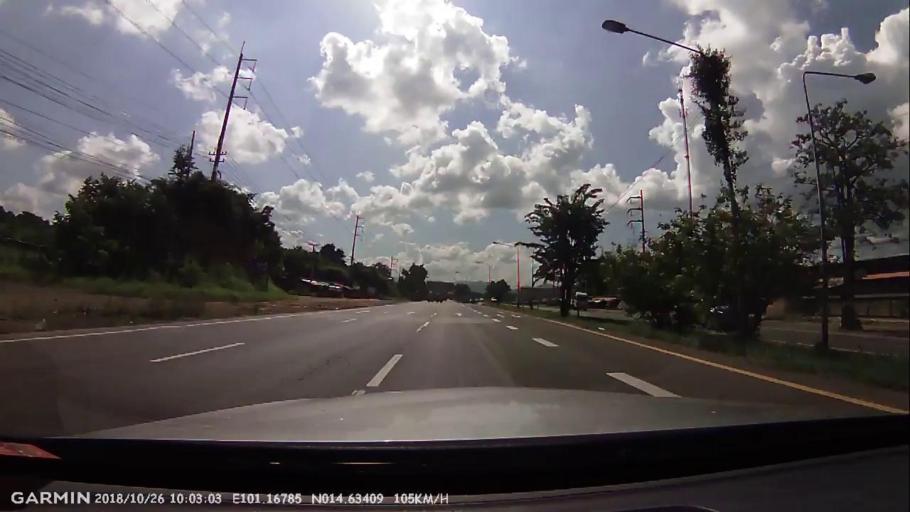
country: TH
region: Sara Buri
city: Muak Lek
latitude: 14.6340
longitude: 101.1679
